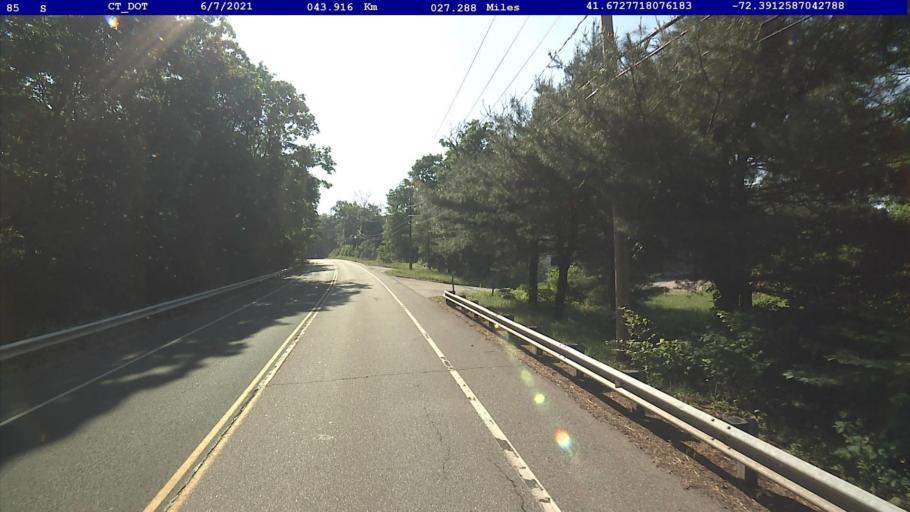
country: US
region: Connecticut
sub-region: Tolland County
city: Hebron
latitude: 41.6726
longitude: -72.3914
